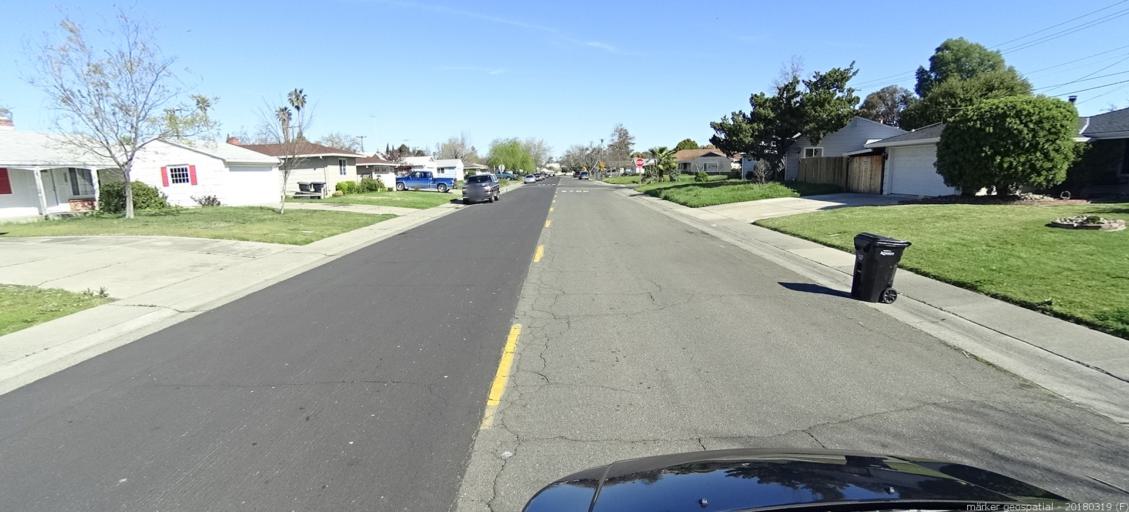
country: US
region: California
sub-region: Sacramento County
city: Parkway
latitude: 38.4882
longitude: -121.4414
